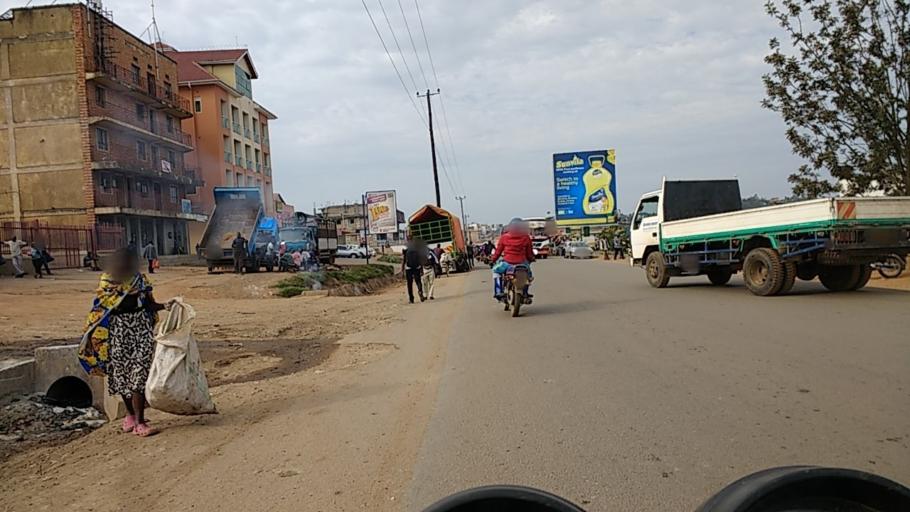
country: UG
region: Western Region
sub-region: Mbarara District
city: Mbarara
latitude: -0.5962
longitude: 30.6649
